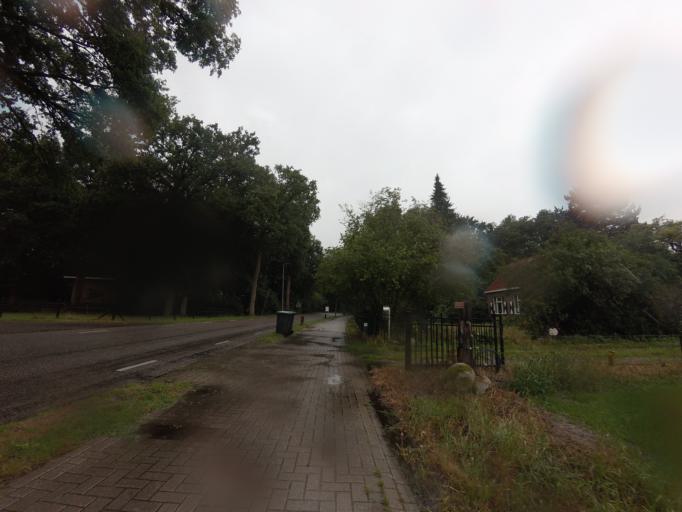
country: NL
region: Drenthe
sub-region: Gemeente Hoogeveen
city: Hoogeveen
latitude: 52.6450
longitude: 6.4292
